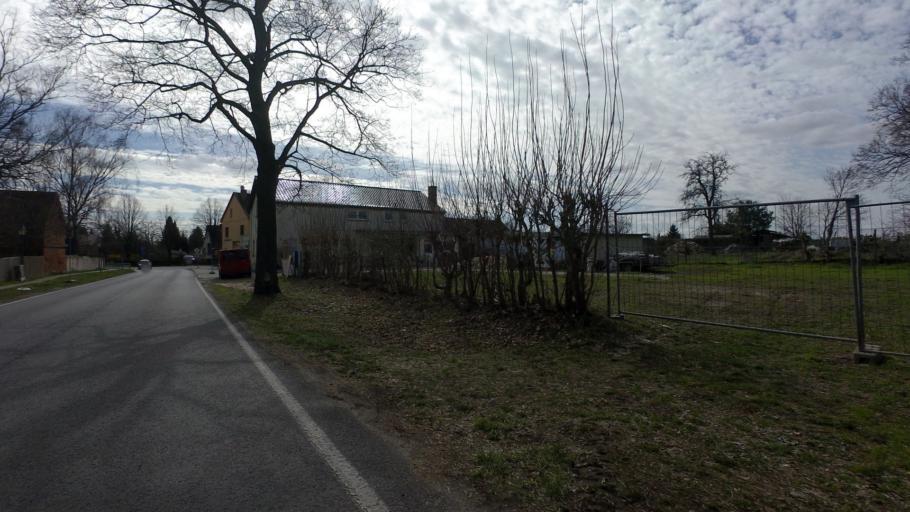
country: DE
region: Berlin
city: Buchholz
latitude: 52.6545
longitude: 13.4344
